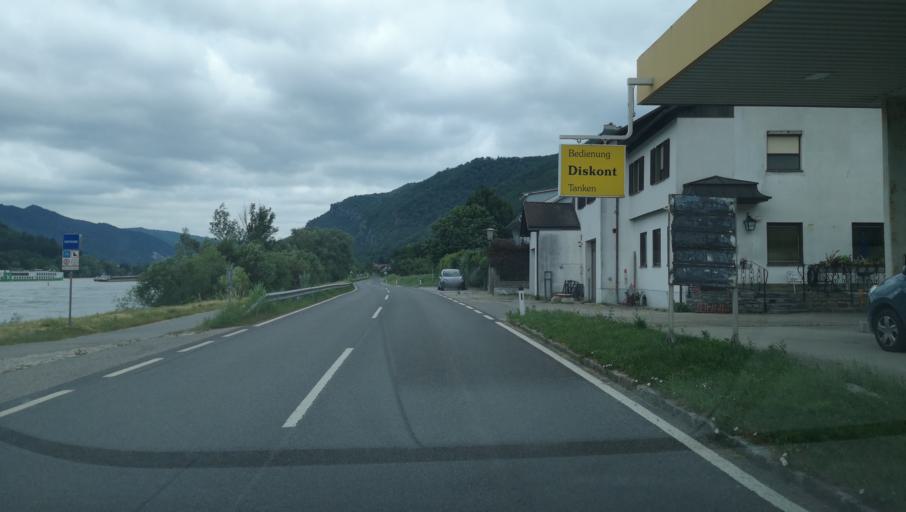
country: AT
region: Lower Austria
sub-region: Politischer Bezirk Krems
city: Aggsbach
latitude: 48.3015
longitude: 15.4108
